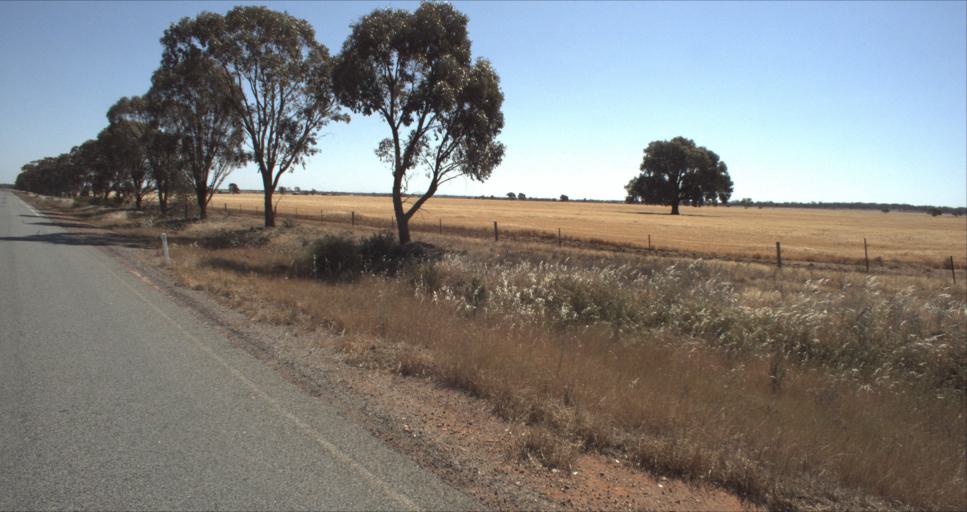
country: AU
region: New South Wales
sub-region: Leeton
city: Leeton
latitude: -34.4935
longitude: 146.4605
